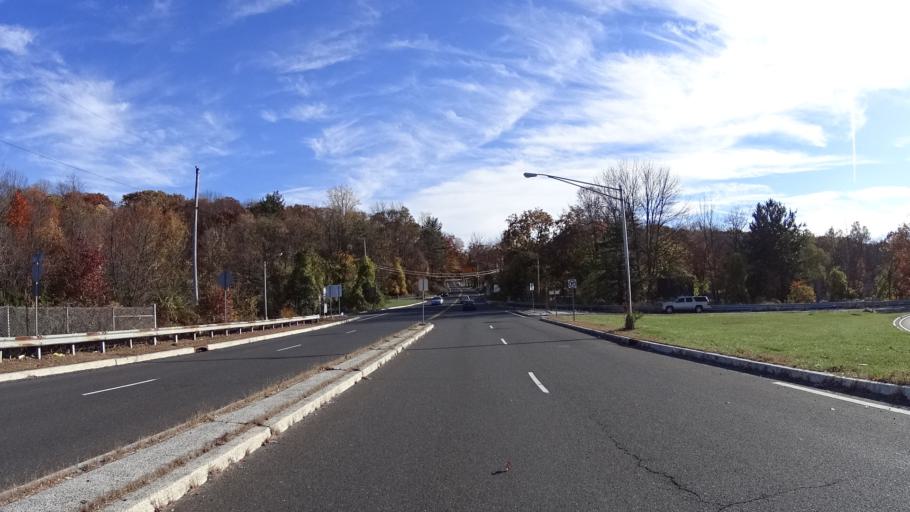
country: US
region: New Jersey
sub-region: Somerset County
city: Watchung
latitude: 40.6509
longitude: -74.4544
